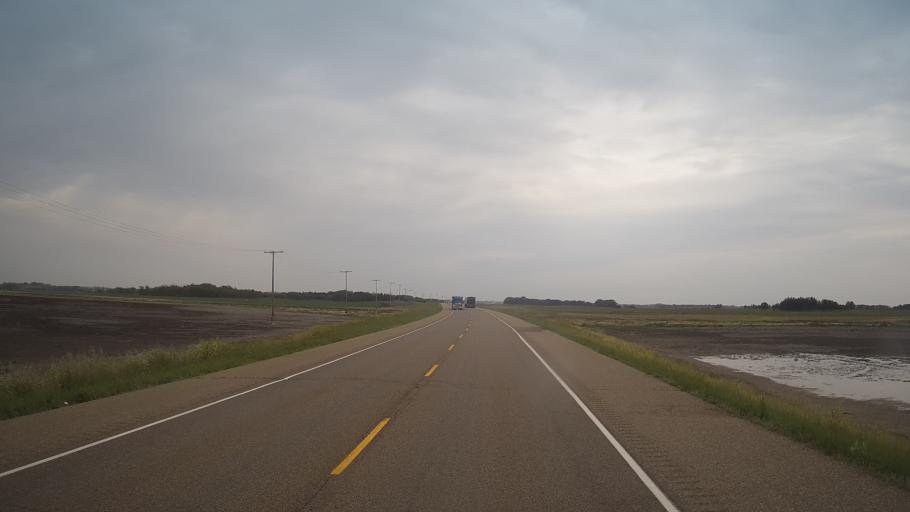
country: CA
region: Saskatchewan
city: Langham
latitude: 52.1294
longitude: -107.1038
